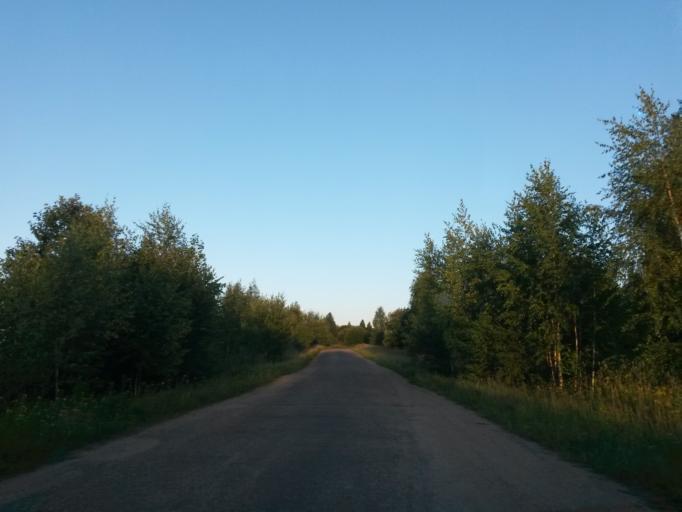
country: RU
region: Jaroslavl
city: Gavrilov-Yam
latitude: 57.3506
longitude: 40.0389
